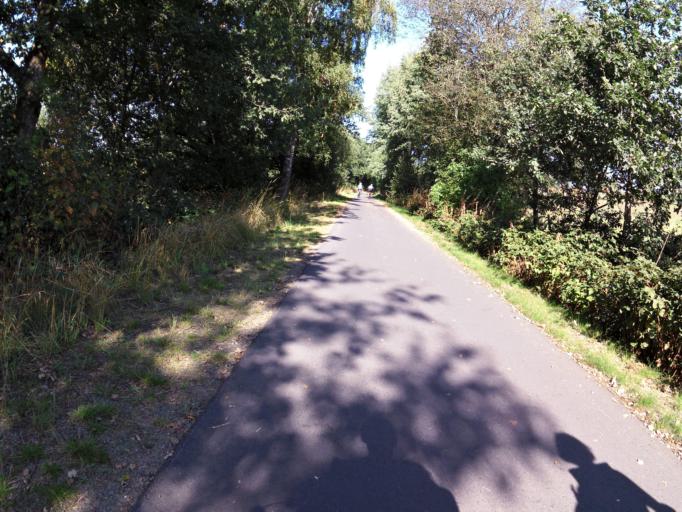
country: BE
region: Wallonia
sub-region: Province de Liege
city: Waimes
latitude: 50.3928
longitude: 6.1232
